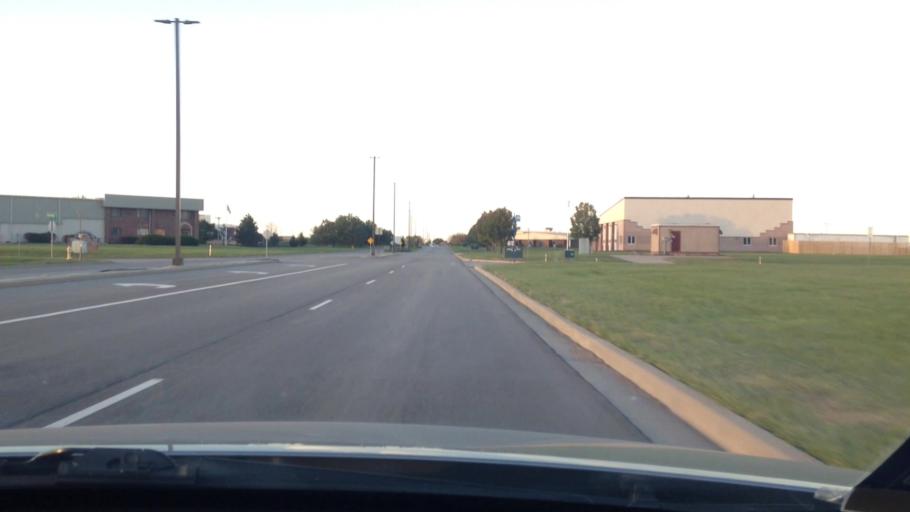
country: US
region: Kansas
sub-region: Johnson County
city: Gardner
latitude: 38.8294
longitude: -94.9080
